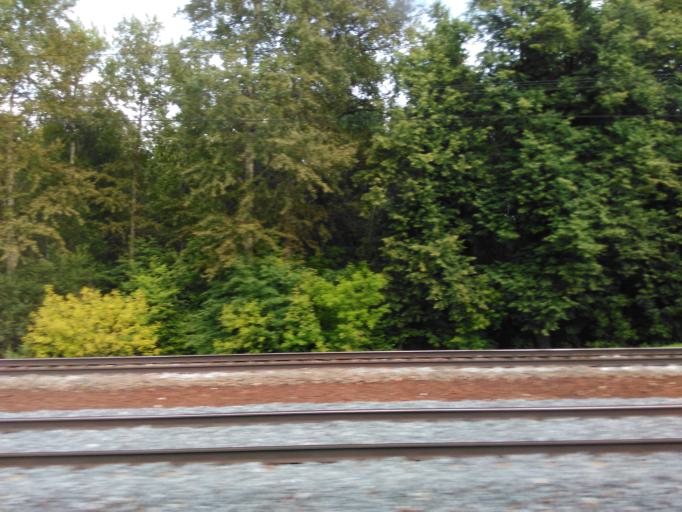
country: RU
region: Moscow
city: Rostokino
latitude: 55.8351
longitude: 37.6706
